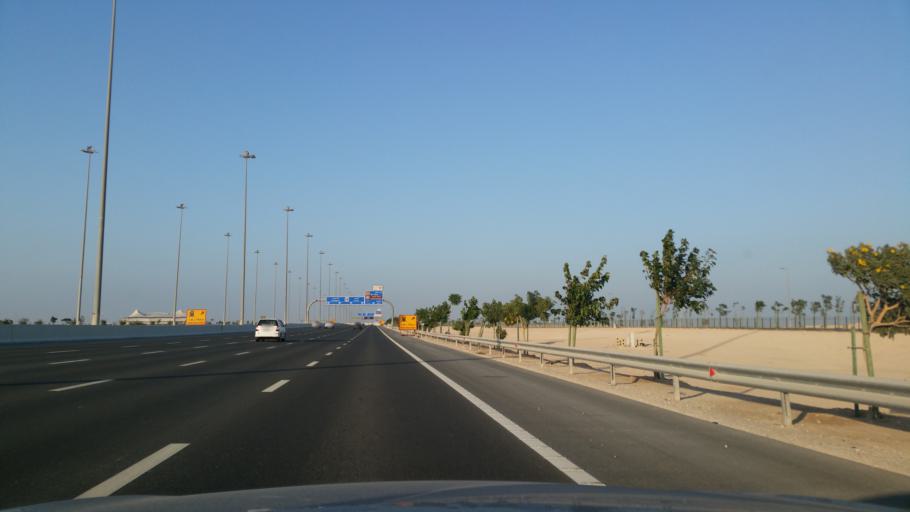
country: QA
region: Baladiyat az Za`ayin
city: Az Za`ayin
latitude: 25.6195
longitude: 51.4842
